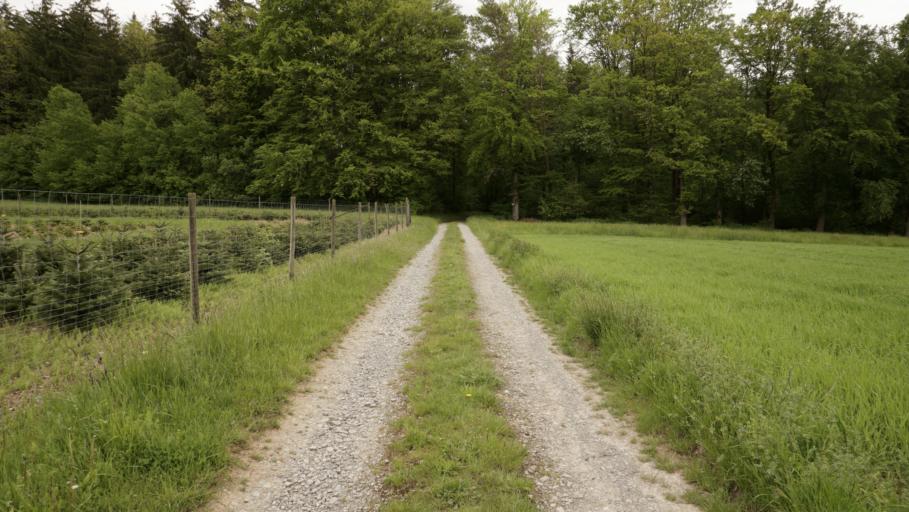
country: DE
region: Baden-Wuerttemberg
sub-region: Karlsruhe Region
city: Mosbach
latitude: 49.3695
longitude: 9.1641
